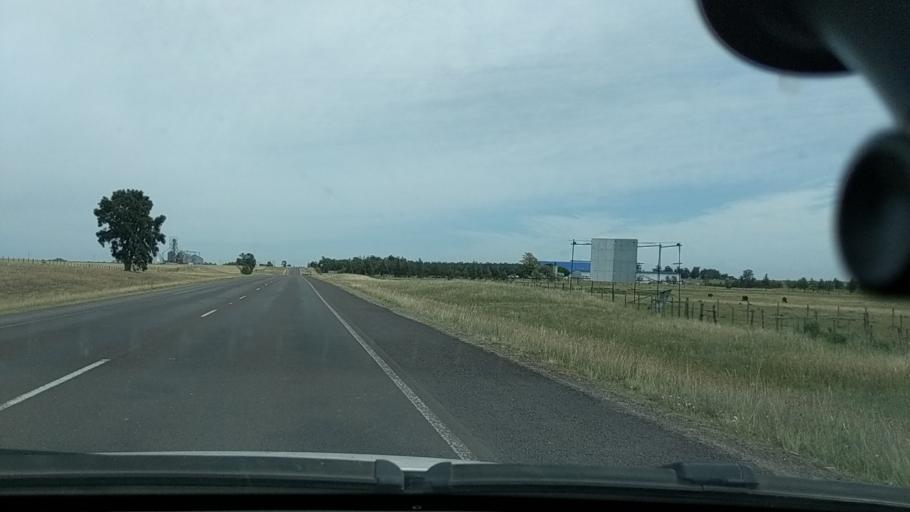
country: UY
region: Durazno
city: Durazno
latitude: -33.4562
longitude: -56.4677
